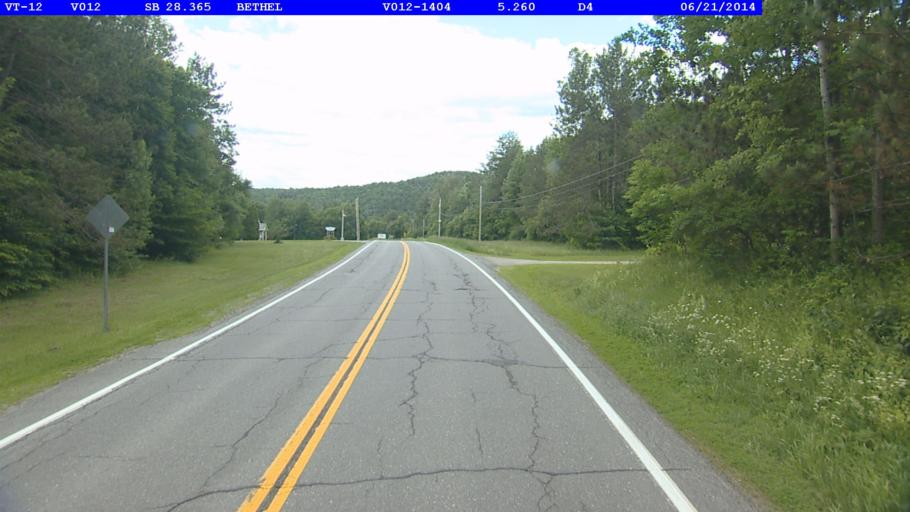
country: US
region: Vermont
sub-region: Orange County
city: Randolph
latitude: 43.8717
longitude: -72.6465
